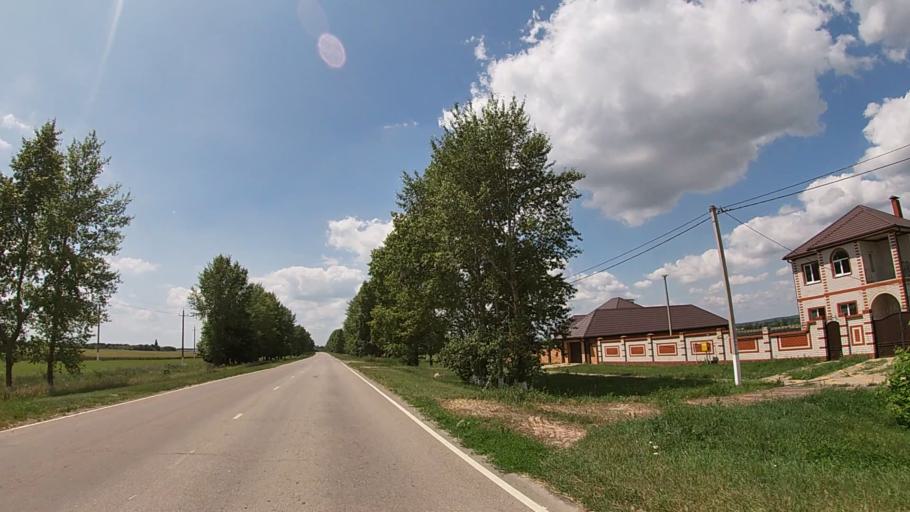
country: RU
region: Belgorod
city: Grayvoron
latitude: 50.4406
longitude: 35.6131
